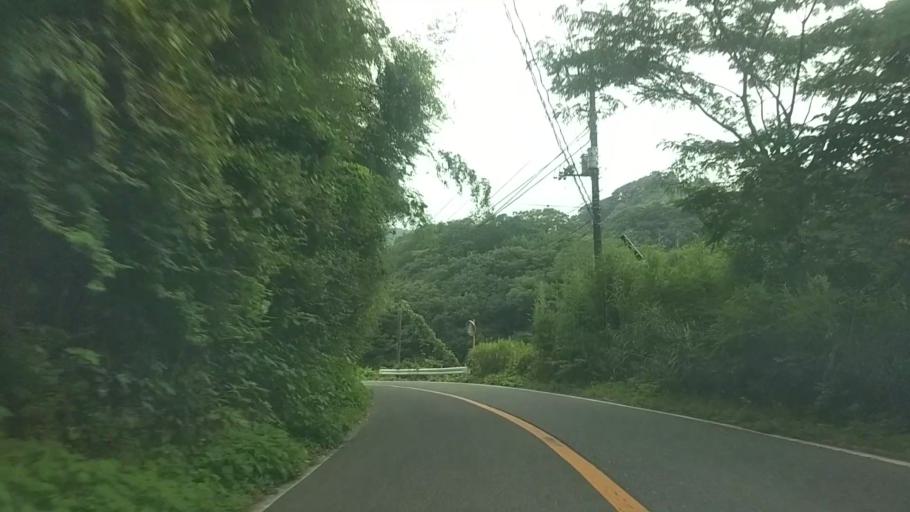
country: JP
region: Chiba
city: Tateyama
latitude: 35.1427
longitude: 139.8953
